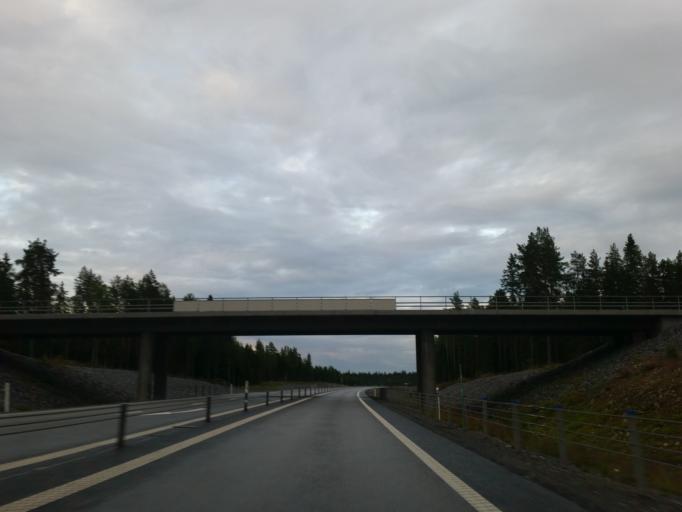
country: SE
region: Vaesterbotten
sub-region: Umea Kommun
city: Umea
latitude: 63.8584
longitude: 20.2377
